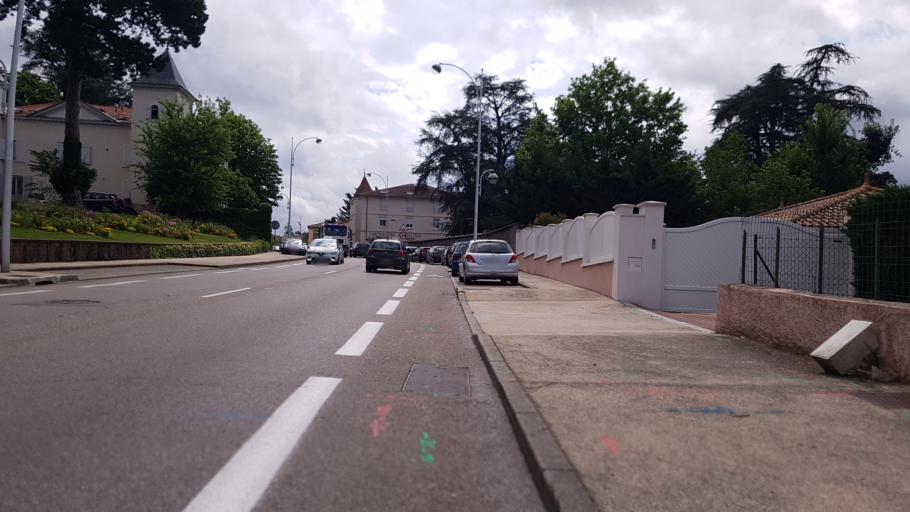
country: FR
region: Rhone-Alpes
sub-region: Departement du Rhone
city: Genas
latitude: 45.7326
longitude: 4.9937
